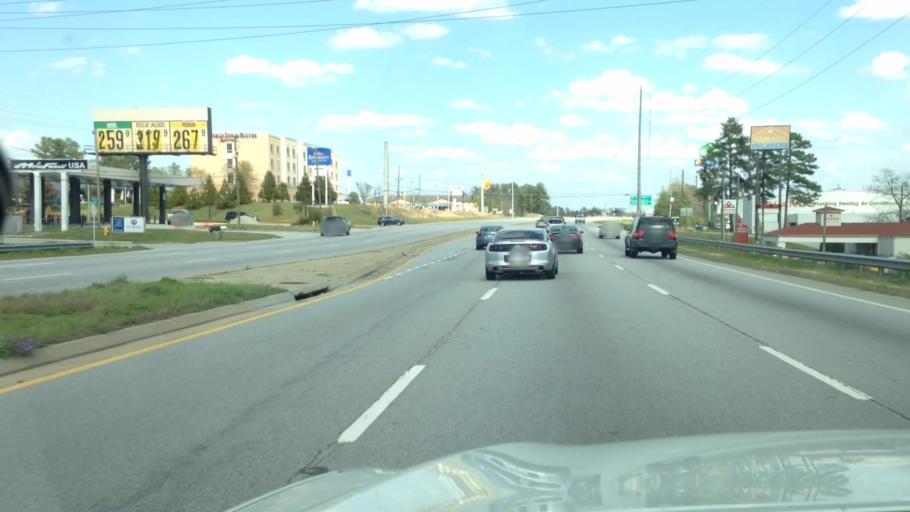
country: US
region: Georgia
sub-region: Columbia County
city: Martinez
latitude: 33.4487
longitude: -82.0821
